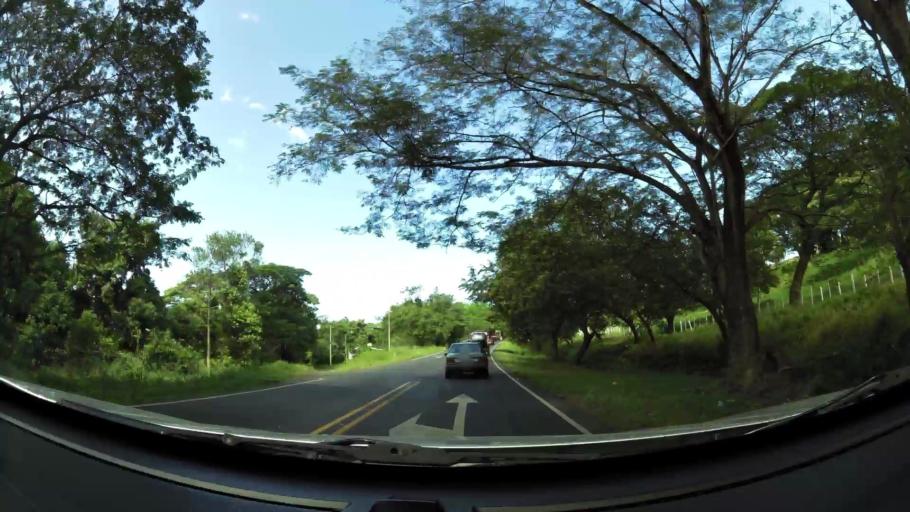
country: CR
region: Guanacaste
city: Juntas
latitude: 10.3122
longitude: -85.0425
